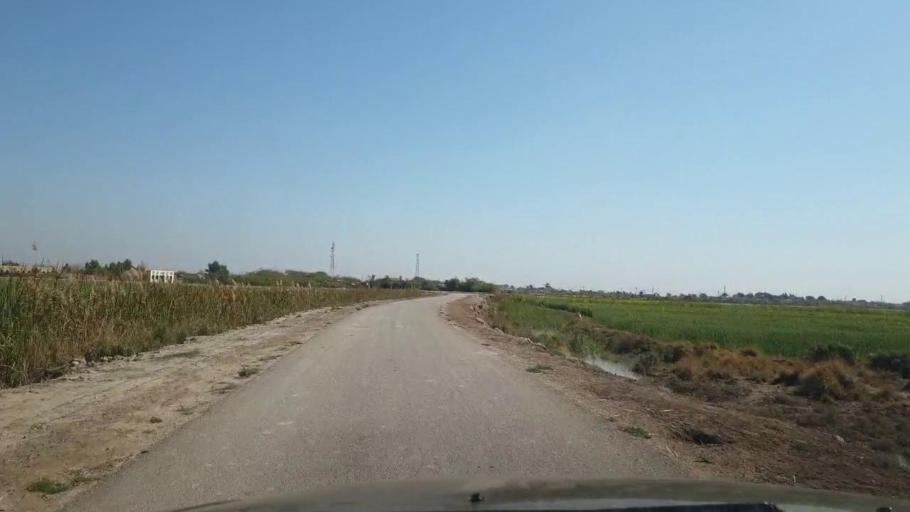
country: PK
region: Sindh
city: Mirpur Khas
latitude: 25.5695
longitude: 69.0588
